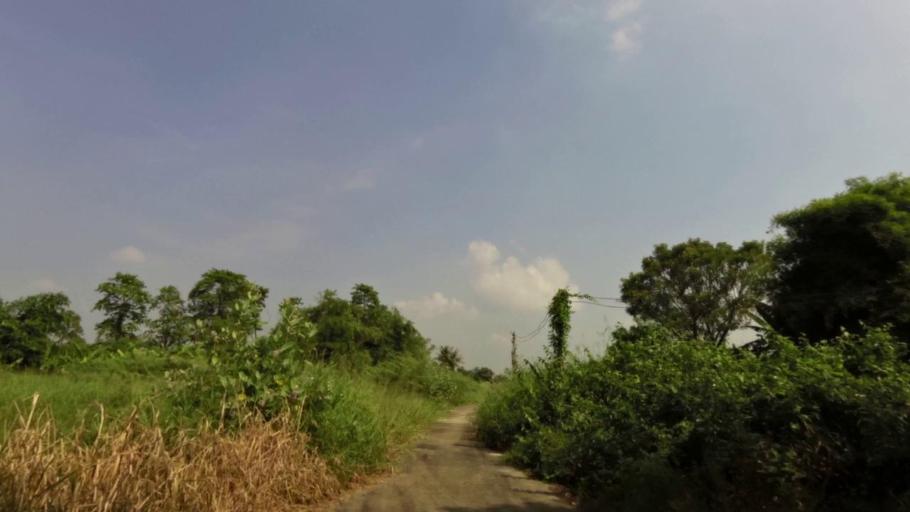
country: TH
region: Ang Thong
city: Wiset Chaichan
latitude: 14.6097
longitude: 100.3923
